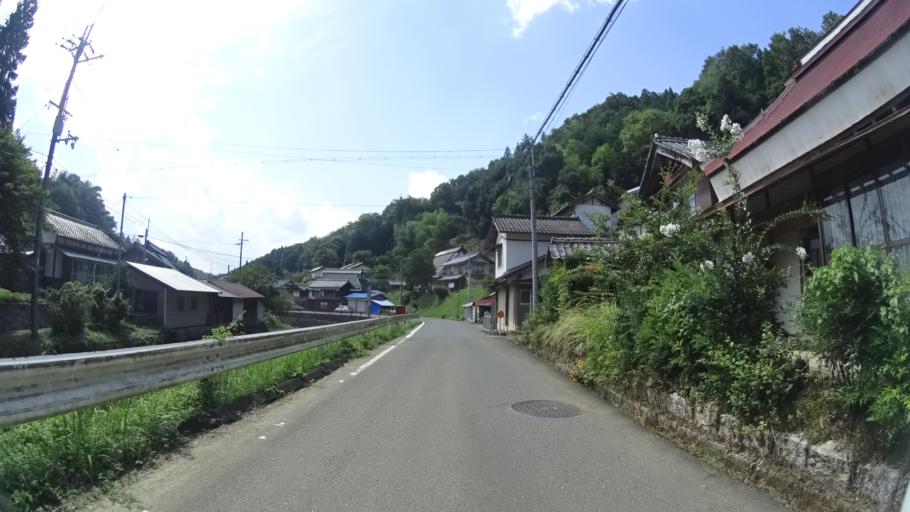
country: JP
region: Kyoto
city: Maizuru
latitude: 35.3770
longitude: 135.3487
